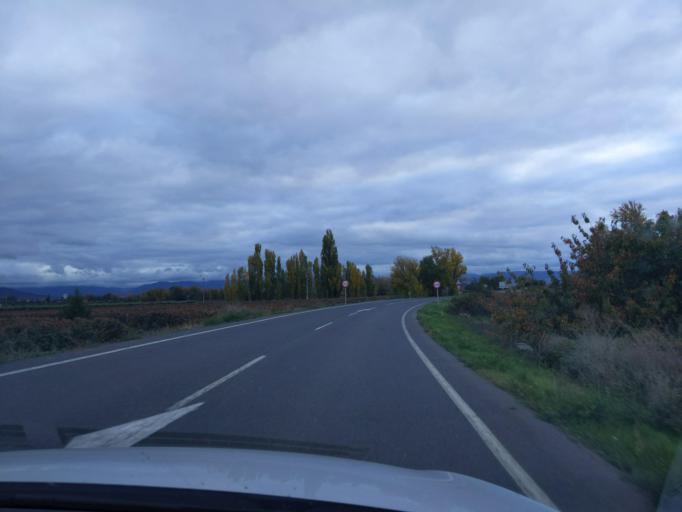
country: ES
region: La Rioja
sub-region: Provincia de La Rioja
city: Urunuela
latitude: 42.4406
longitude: -2.7013
